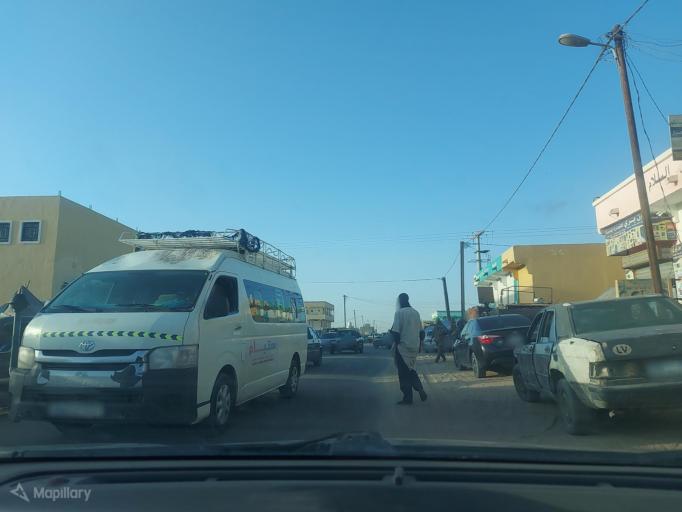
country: MR
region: Nouakchott
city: Nouakchott
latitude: 18.0656
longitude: -15.8925
